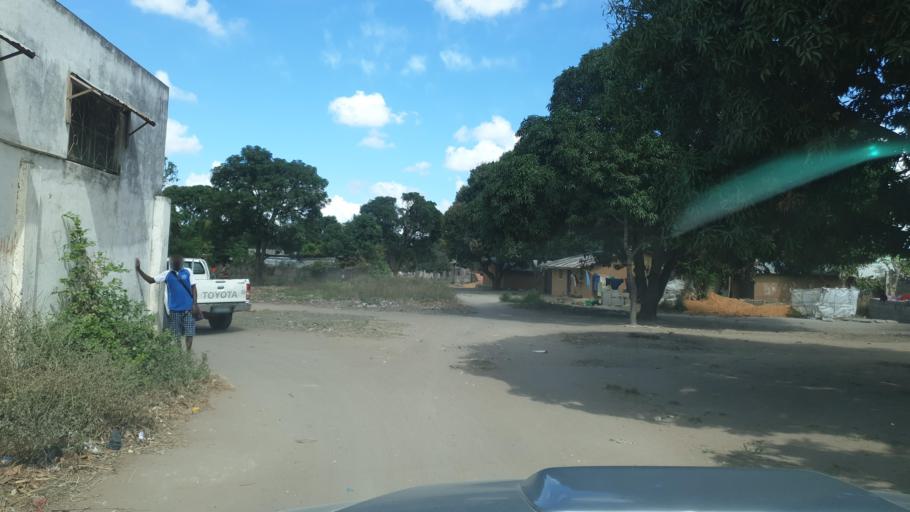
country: MZ
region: Nampula
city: Nacala
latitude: -14.5675
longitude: 40.7005
